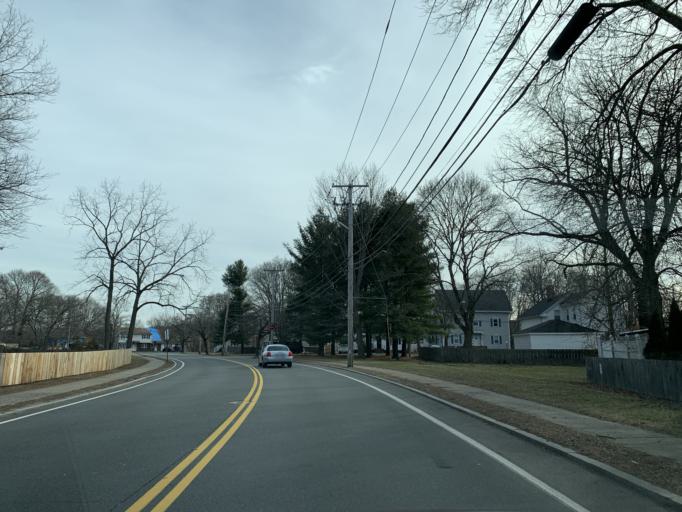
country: US
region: Massachusetts
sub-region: Essex County
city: Saugus
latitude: 42.4688
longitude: -71.0094
